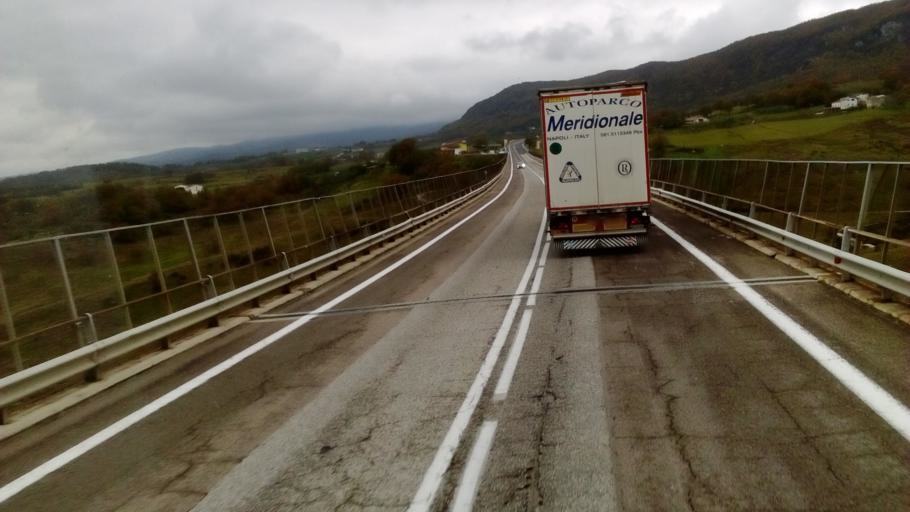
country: IT
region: Molise
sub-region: Provincia di Isernia
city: Civitanova del Sannio
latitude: 41.7051
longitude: 14.4171
